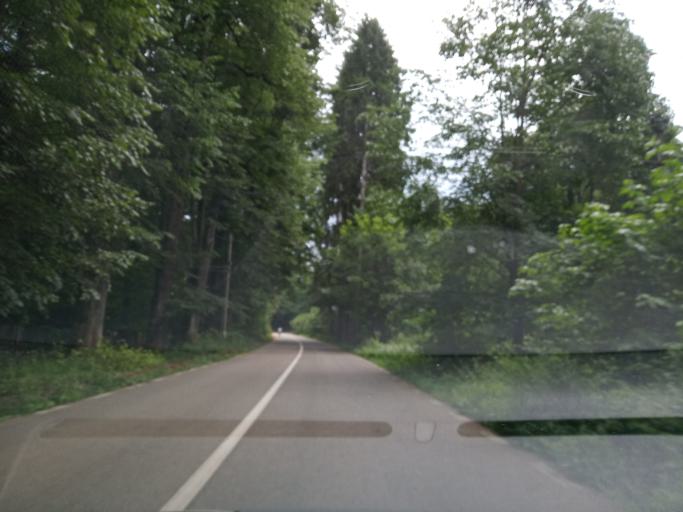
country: RO
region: Gorj
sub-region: Comuna Tismana
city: Pocruia
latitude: 45.0732
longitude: 22.9328
